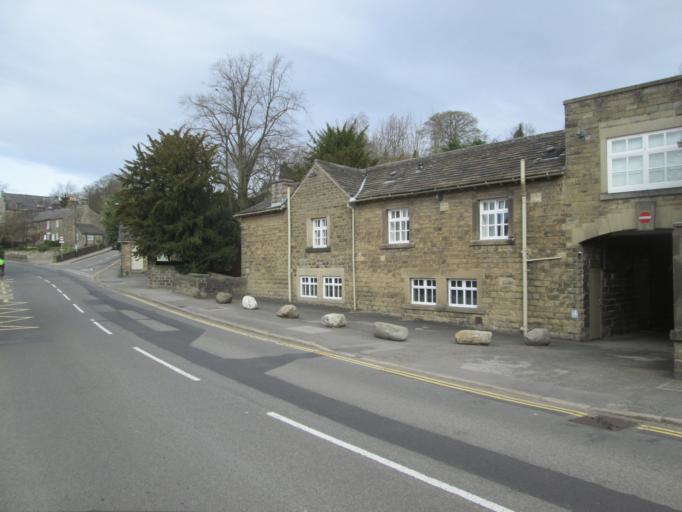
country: GB
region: England
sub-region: Derbyshire
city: Hathersage
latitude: 53.3301
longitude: -1.6566
